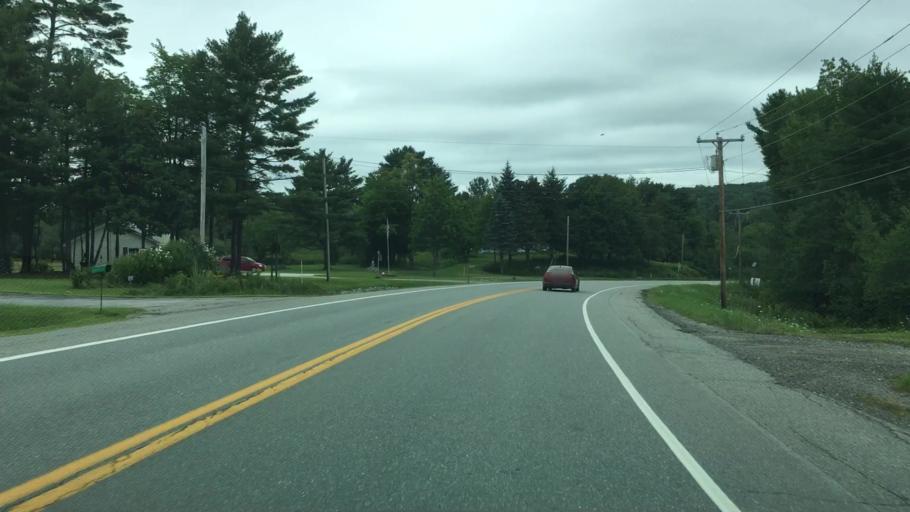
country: US
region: Maine
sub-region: Waldo County
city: Frankfort
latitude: 44.6210
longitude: -68.8705
